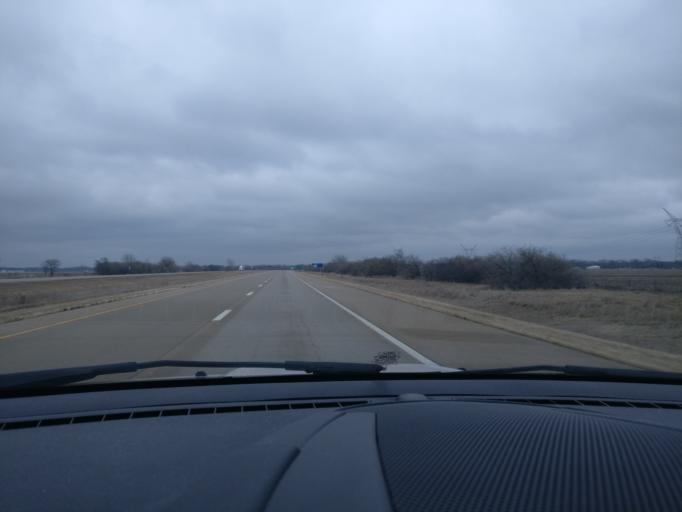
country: US
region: Illinois
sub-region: Whiteside County
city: Sterling
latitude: 41.7653
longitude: -89.8071
